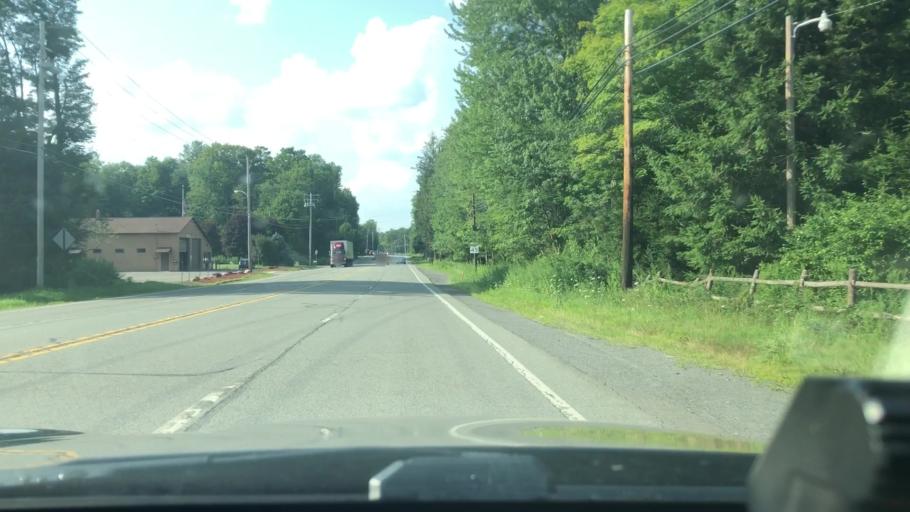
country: US
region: Pennsylvania
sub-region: Lackawanna County
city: Moscow
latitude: 41.2550
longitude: -75.5041
